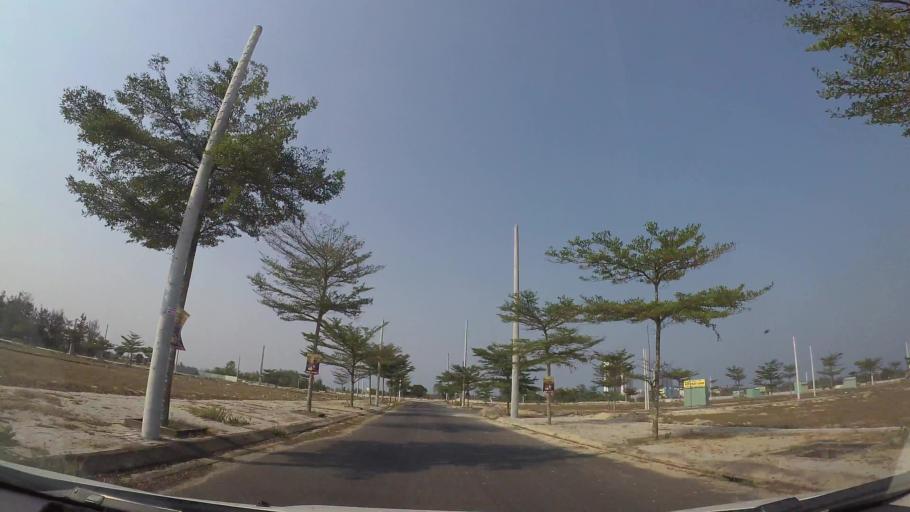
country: VN
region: Da Nang
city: Ngu Hanh Son
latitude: 15.9560
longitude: 108.2733
